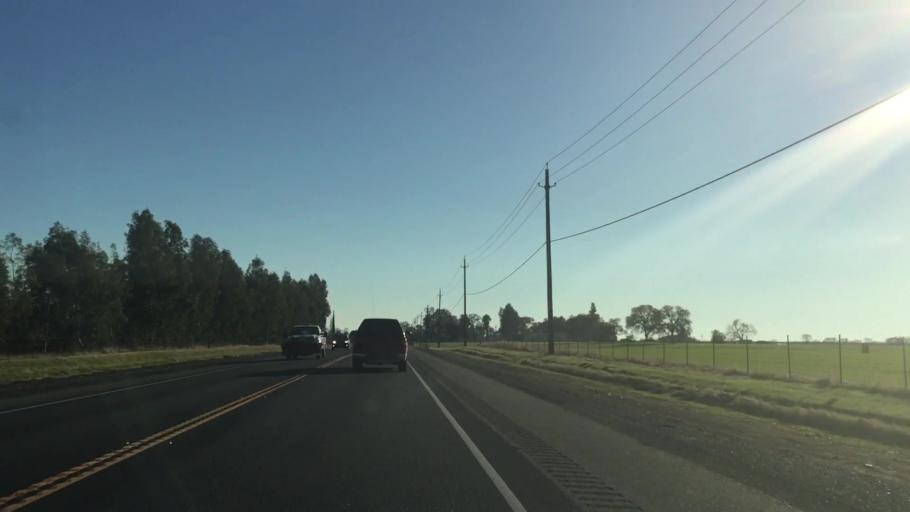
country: US
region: California
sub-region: Butte County
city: Palermo
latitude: 39.4130
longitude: -121.6050
